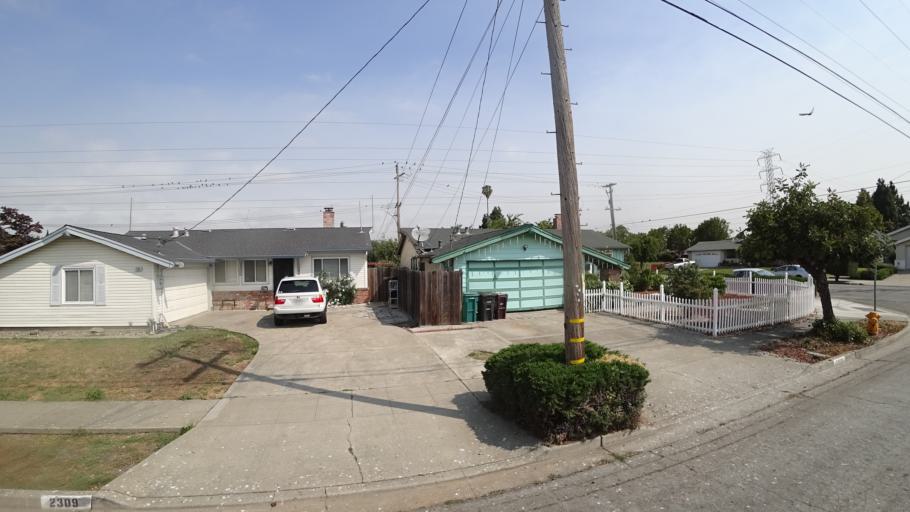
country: US
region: California
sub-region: Alameda County
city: Hayward
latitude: 37.6331
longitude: -122.0992
